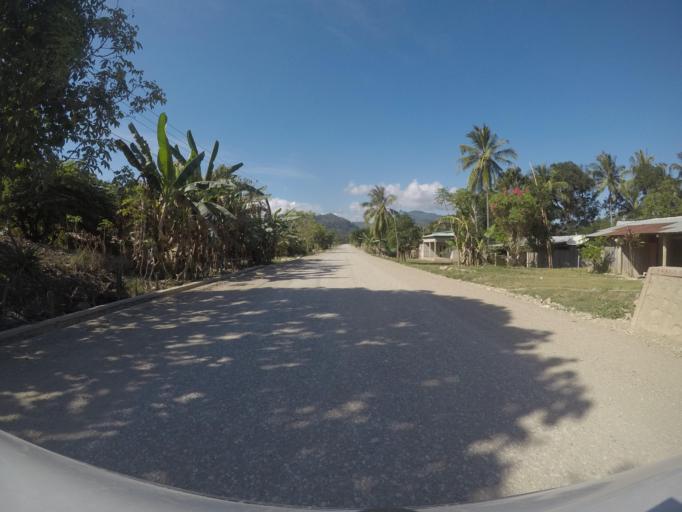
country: TL
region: Viqueque
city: Viqueque
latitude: -8.8139
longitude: 126.5366
